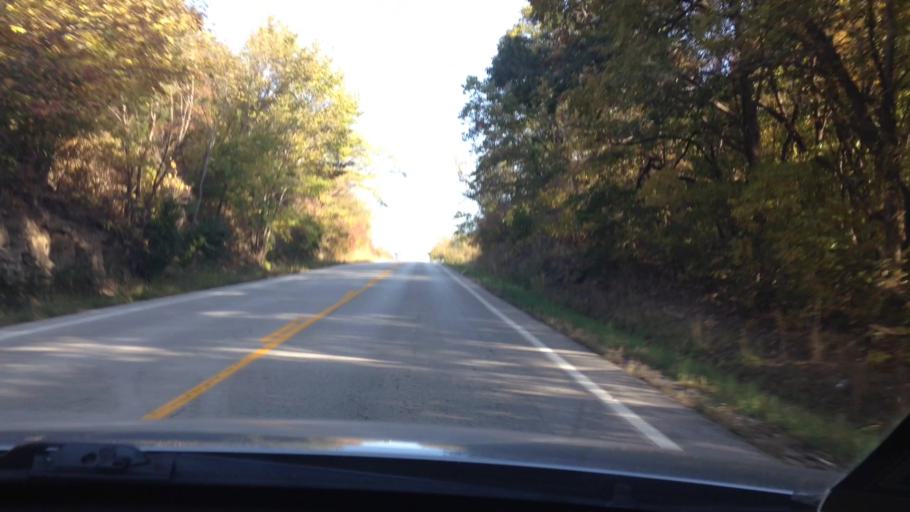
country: US
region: Missouri
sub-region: Platte County
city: Weatherby Lake
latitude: 39.2348
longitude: -94.7919
